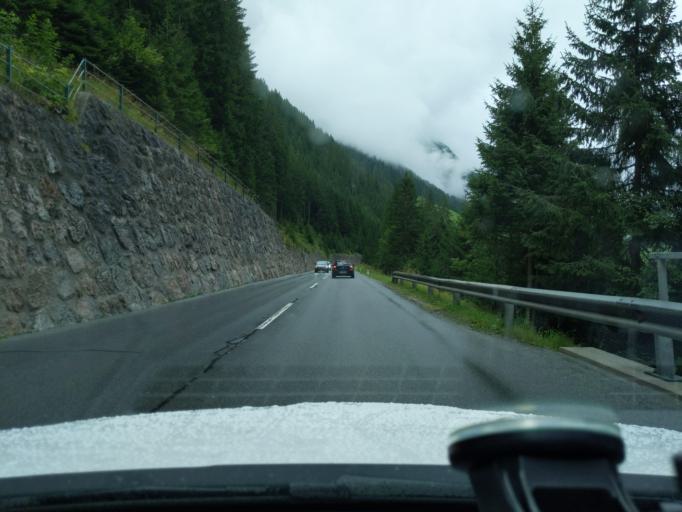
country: AT
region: Tyrol
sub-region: Politischer Bezirk Innsbruck Land
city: Schmirn
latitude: 47.1215
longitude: 11.6916
